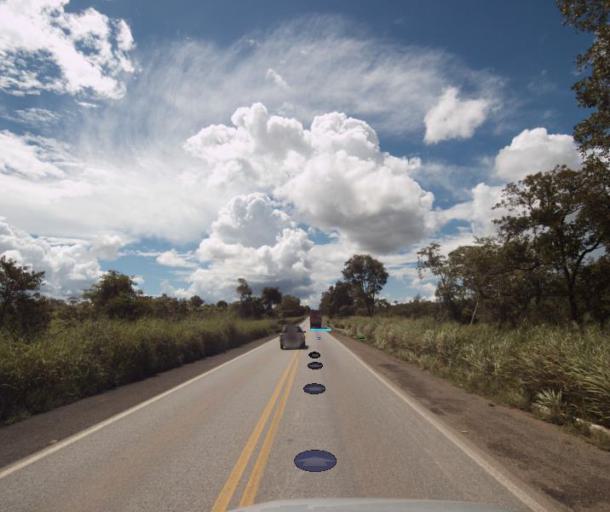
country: BR
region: Goias
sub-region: Uruacu
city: Uruacu
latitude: -14.0749
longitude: -49.0972
